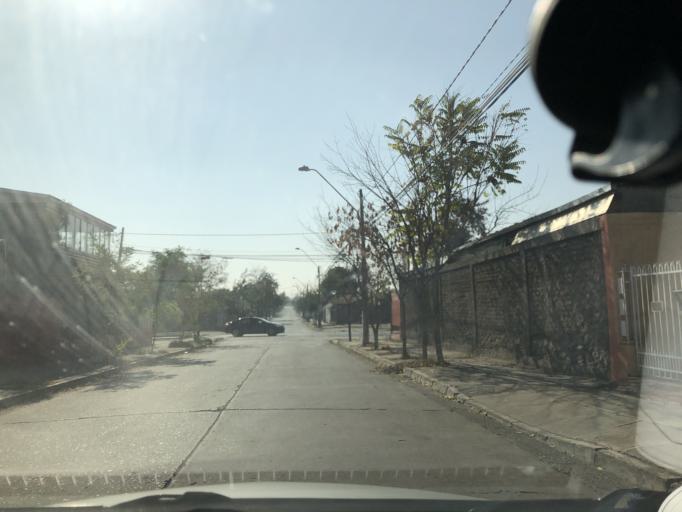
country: CL
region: Santiago Metropolitan
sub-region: Provincia de Cordillera
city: Puente Alto
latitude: -33.6170
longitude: -70.5643
